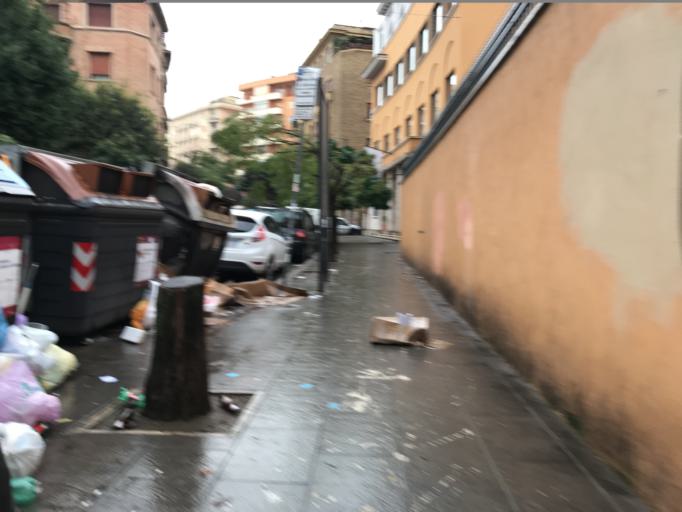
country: IT
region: Latium
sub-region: Citta metropolitana di Roma Capitale
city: Rome
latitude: 41.9132
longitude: 12.5168
